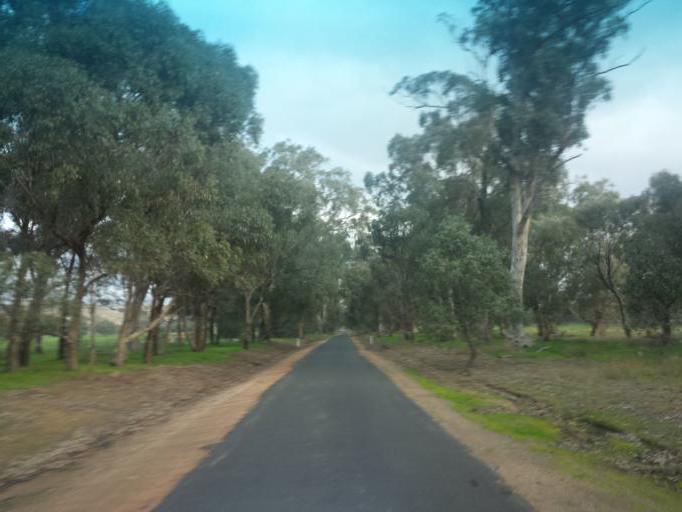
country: AU
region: Victoria
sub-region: Murrindindi
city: Kinglake West
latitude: -36.9212
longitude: 145.2251
